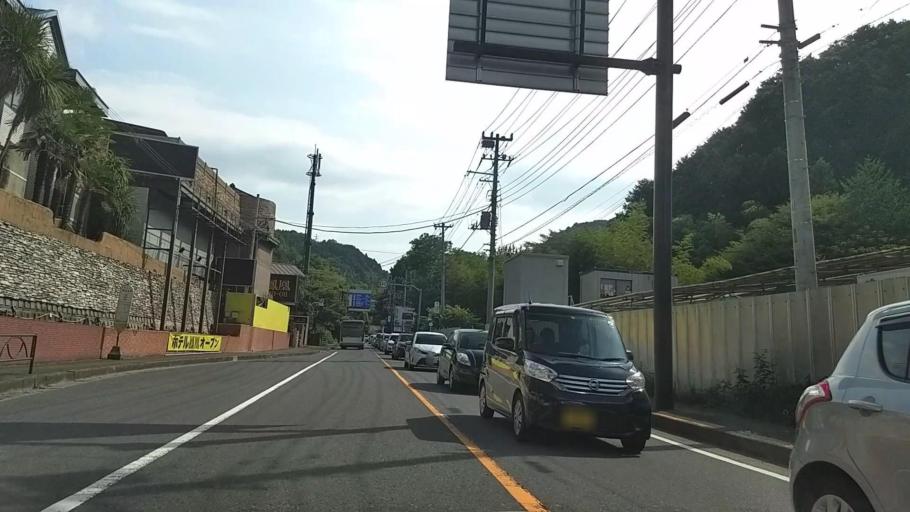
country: JP
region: Tokyo
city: Hachioji
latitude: 35.6215
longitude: 139.2629
